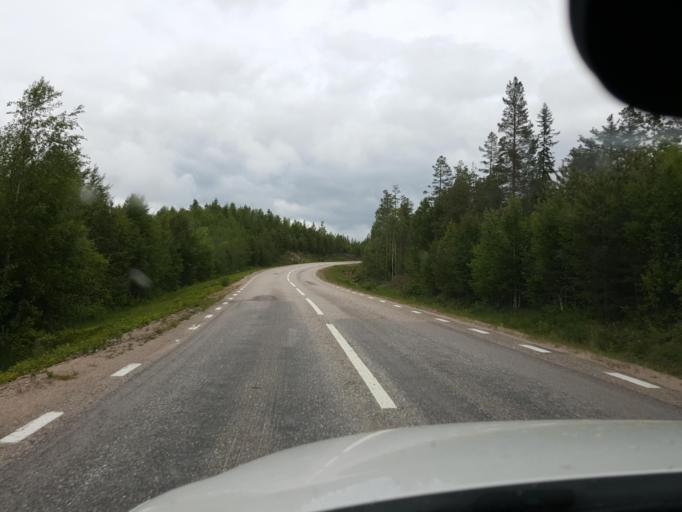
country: SE
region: Gaevleborg
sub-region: Ljusdals Kommun
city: Farila
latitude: 61.7536
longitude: 15.3766
